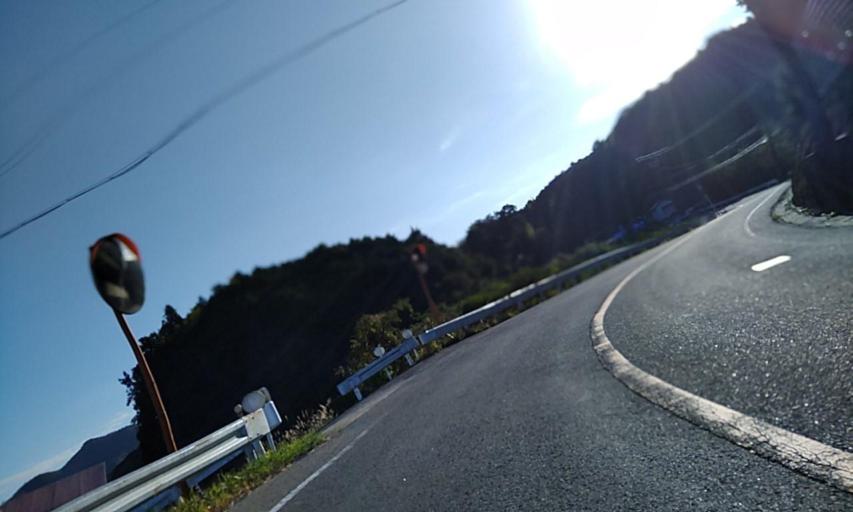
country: JP
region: Wakayama
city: Kainan
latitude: 34.1558
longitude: 135.2875
